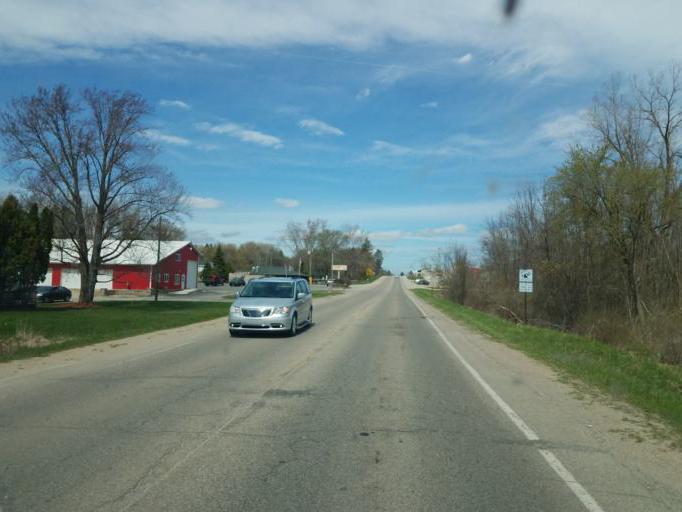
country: US
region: Michigan
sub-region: Isabella County
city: Mount Pleasant
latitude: 43.6287
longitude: -84.7680
